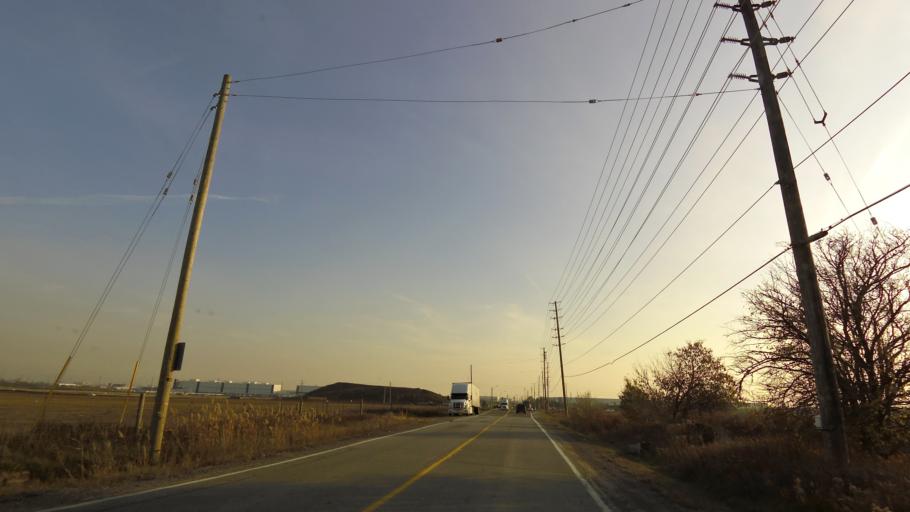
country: CA
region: Ontario
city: Brampton
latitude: 43.7891
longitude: -79.6517
